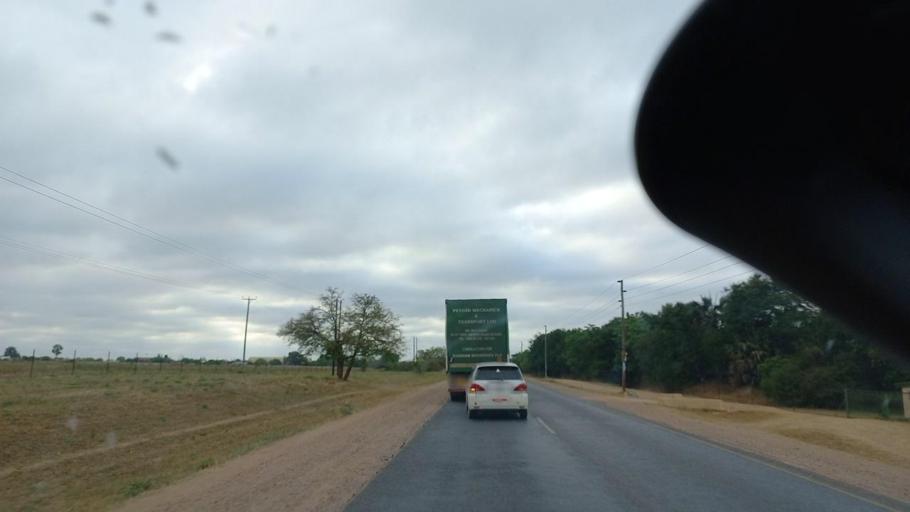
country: ZM
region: Lusaka
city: Chongwe
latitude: -15.3461
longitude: 28.5275
